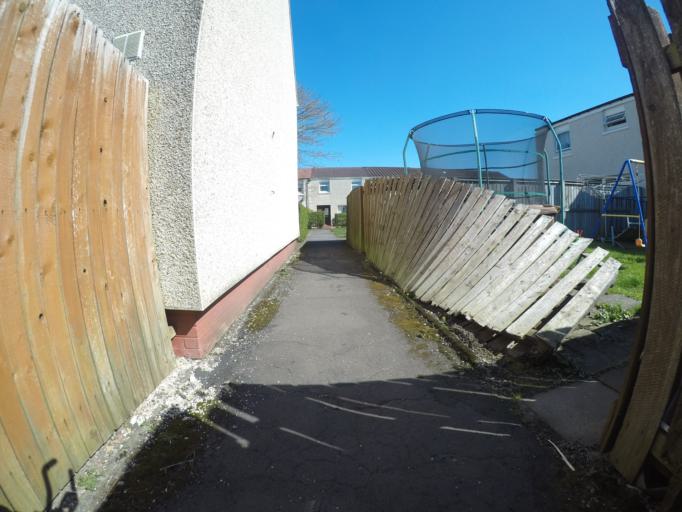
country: GB
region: Scotland
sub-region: North Ayrshire
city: Irvine
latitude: 55.6333
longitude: -4.6652
